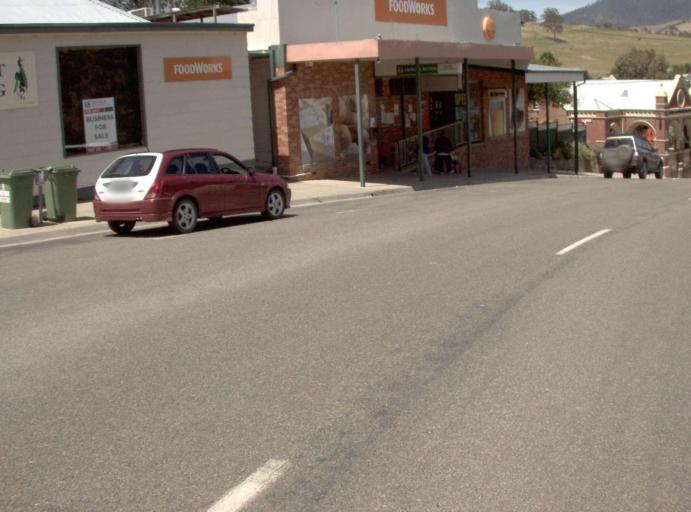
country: AU
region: Victoria
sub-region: Alpine
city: Mount Beauty
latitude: -37.0987
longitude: 147.5943
